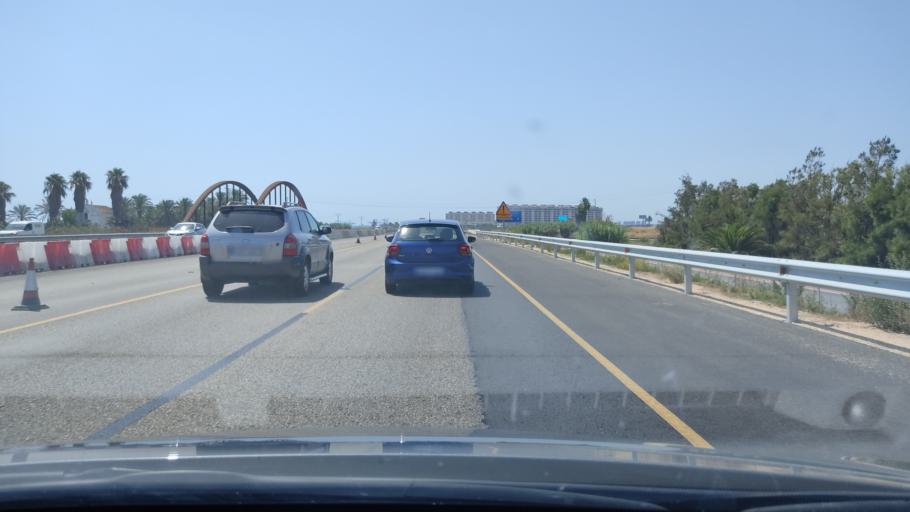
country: ES
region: Valencia
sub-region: Provincia de Valencia
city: Alboraya
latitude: 39.5035
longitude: -0.3261
